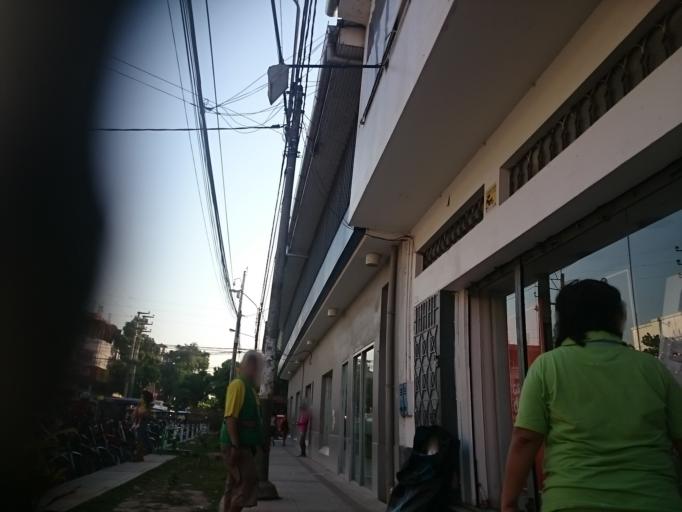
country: PE
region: Ucayali
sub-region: Provincia de Coronel Portillo
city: Pucallpa
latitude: -8.3856
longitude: -74.5307
